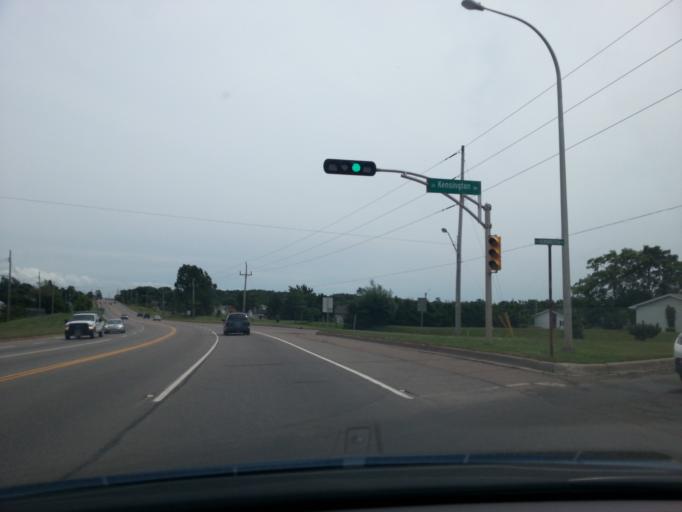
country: CA
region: Prince Edward Island
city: Charlottetown
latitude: 46.2652
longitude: -63.1118
